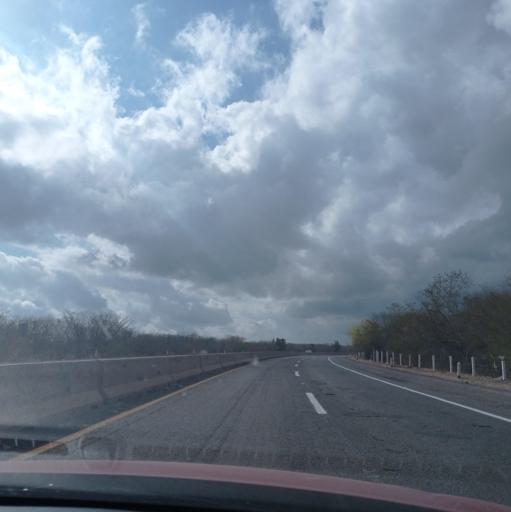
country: MX
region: Sinaloa
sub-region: Navolato
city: Juan Aldama (El Tigre)
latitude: 24.9922
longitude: -107.7735
